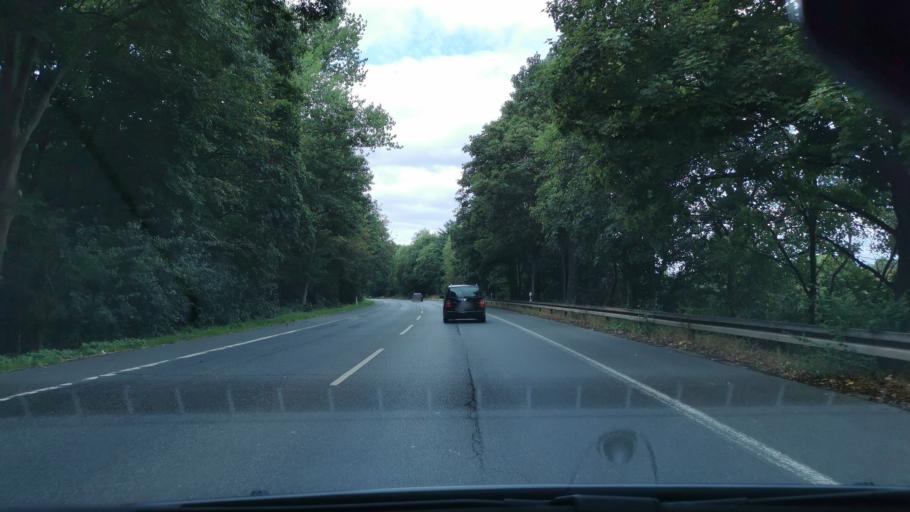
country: DE
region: North Rhine-Westphalia
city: Wesseling
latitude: 50.8668
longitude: 6.9858
